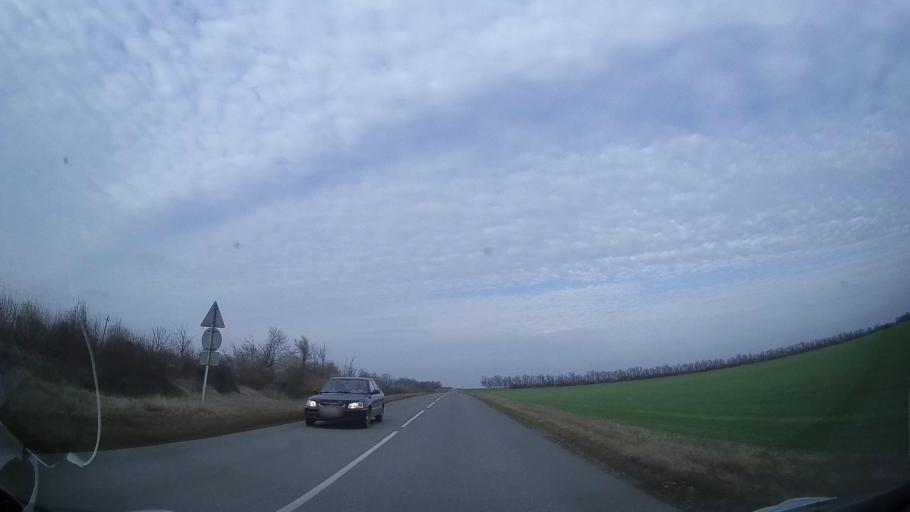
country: RU
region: Rostov
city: Zernograd
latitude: 46.9081
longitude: 40.3390
